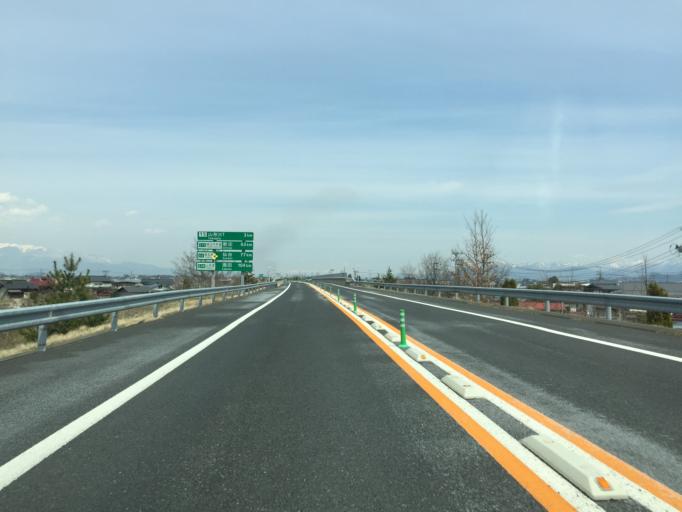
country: JP
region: Yamagata
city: Yamagata-shi
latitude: 38.2815
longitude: 140.2977
